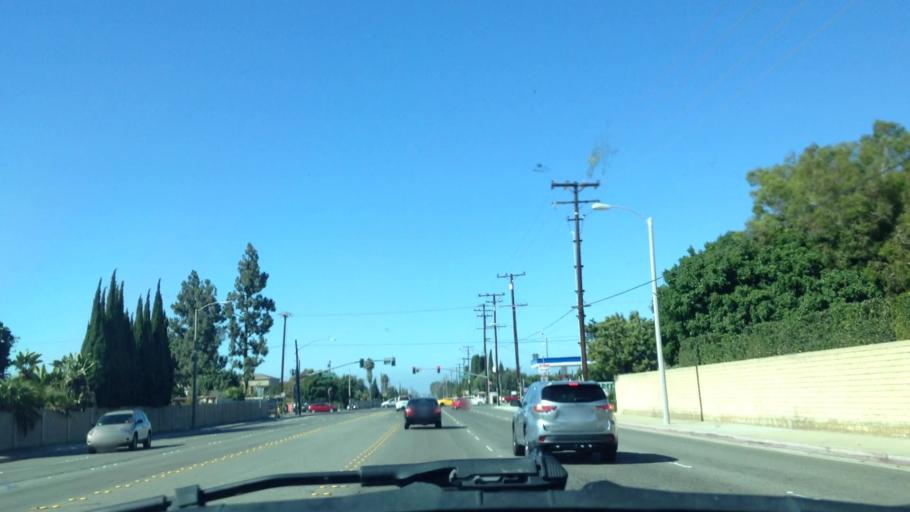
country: US
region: California
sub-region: Orange County
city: Midway City
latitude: 33.7289
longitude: -117.9720
